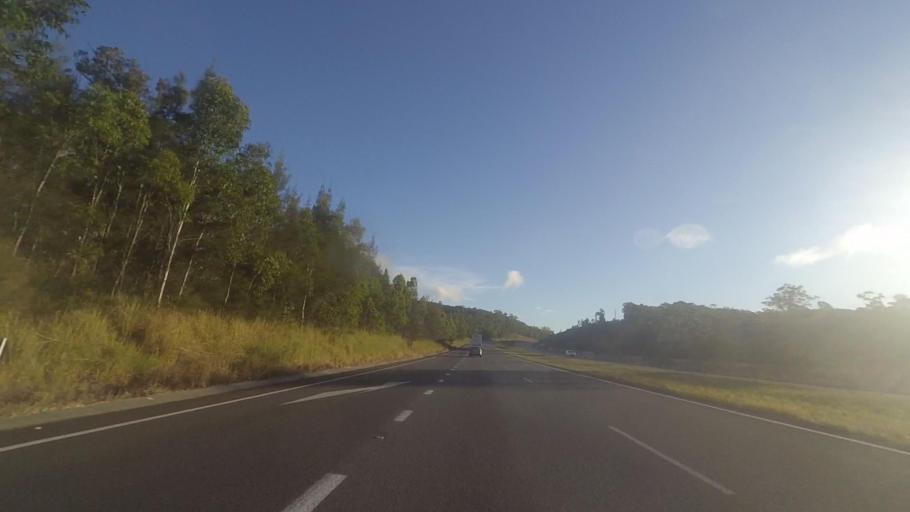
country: AU
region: New South Wales
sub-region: Great Lakes
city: Bulahdelah
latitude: -32.5119
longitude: 152.2105
